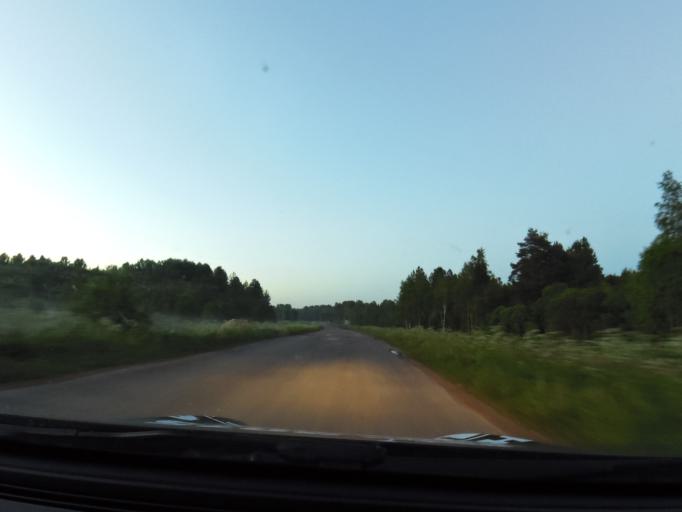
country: RU
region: Vologda
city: Vytegra
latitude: 60.9910
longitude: 36.3582
